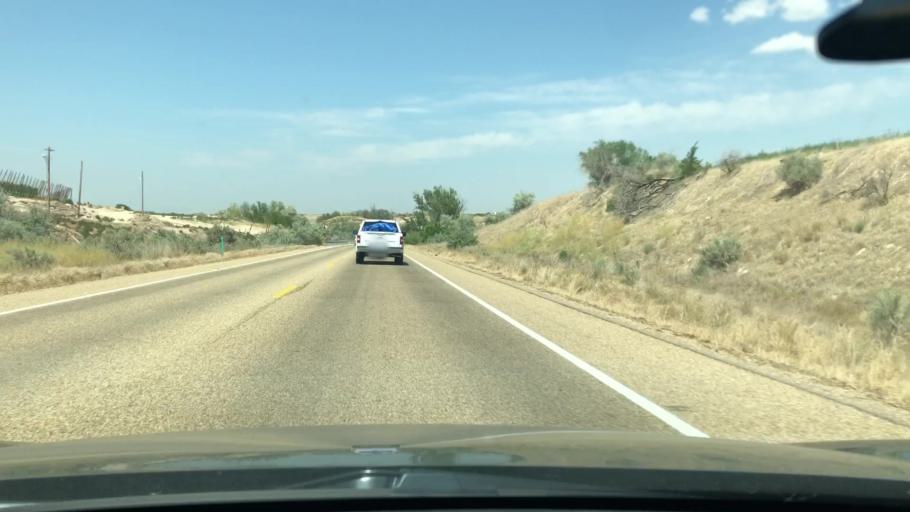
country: US
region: Idaho
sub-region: Canyon County
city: Wilder
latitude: 43.7137
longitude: -116.9118
